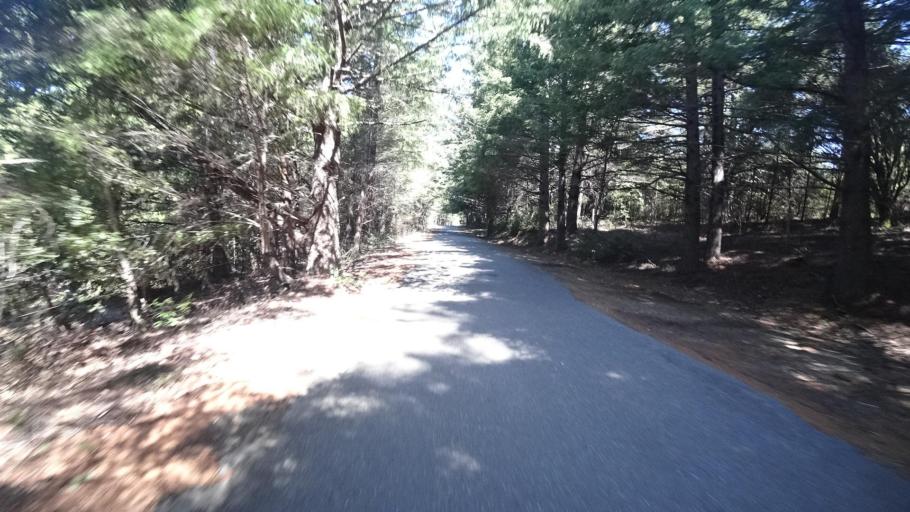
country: US
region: California
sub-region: Humboldt County
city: Redway
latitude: 40.1689
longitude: -124.0857
